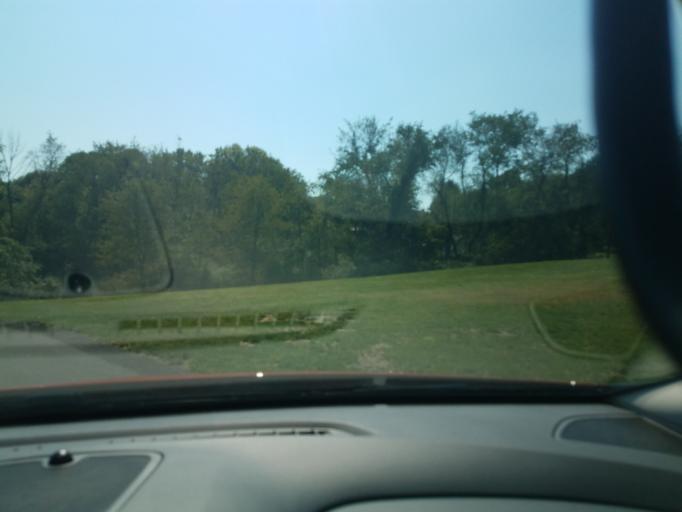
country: US
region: Pennsylvania
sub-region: Allegheny County
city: Franklin Park
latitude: 40.5687
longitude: -80.0724
